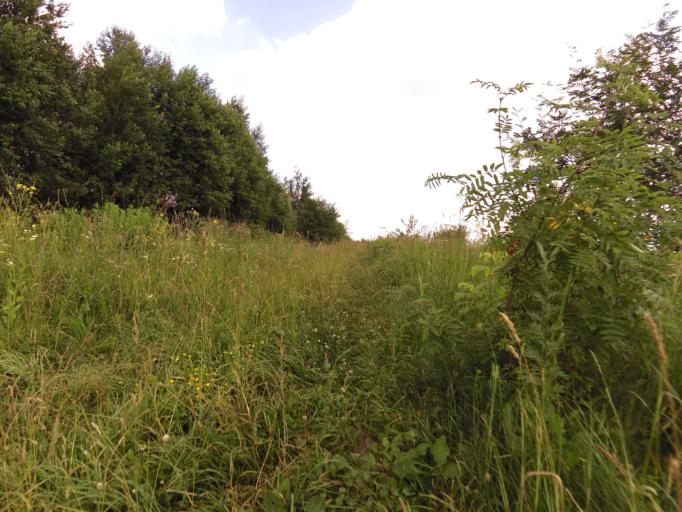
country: LT
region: Vilnius County
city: Pasilaiciai
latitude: 54.7542
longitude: 25.2208
